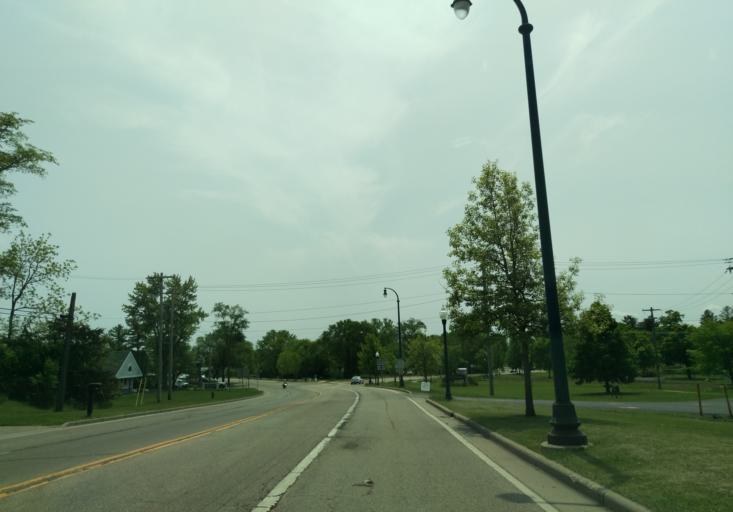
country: US
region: Wisconsin
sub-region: Rock County
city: Evansville
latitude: 42.7864
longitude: -89.2990
